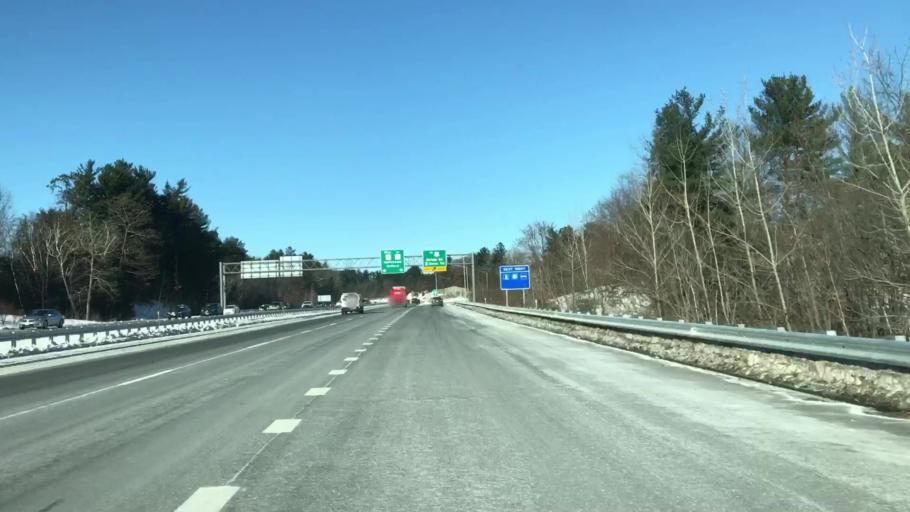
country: US
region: New Hampshire
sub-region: Hillsborough County
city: Bedford
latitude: 42.9539
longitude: -71.4830
